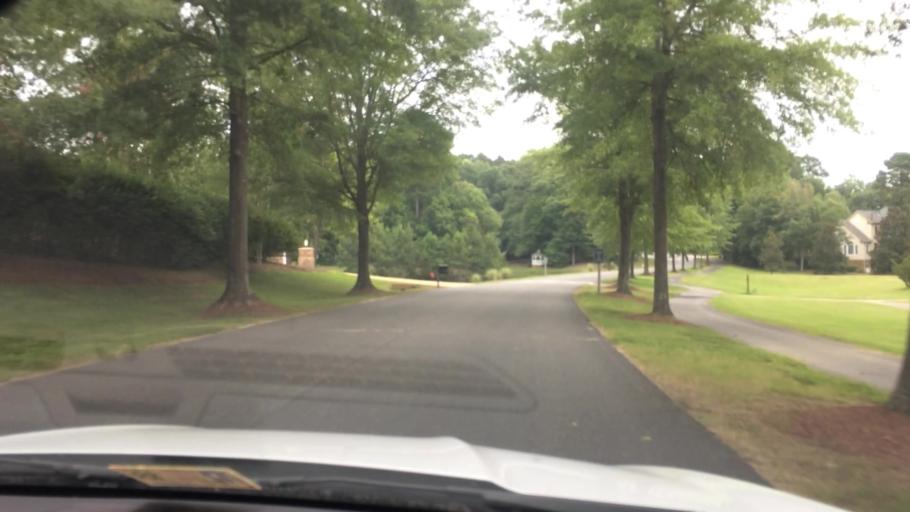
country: US
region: Virginia
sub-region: James City County
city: Williamsburg
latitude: 37.3001
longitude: -76.7953
